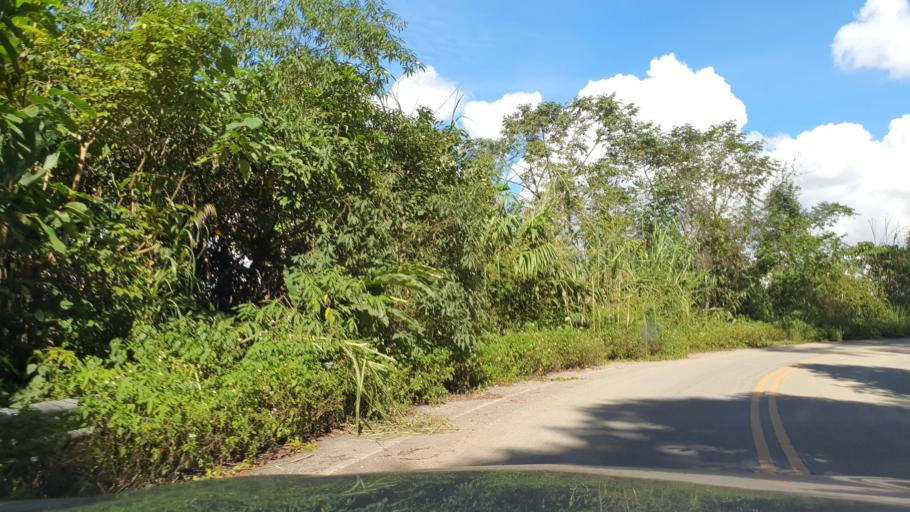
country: TH
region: Chiang Mai
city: Phrao
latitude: 19.3122
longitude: 99.3321
